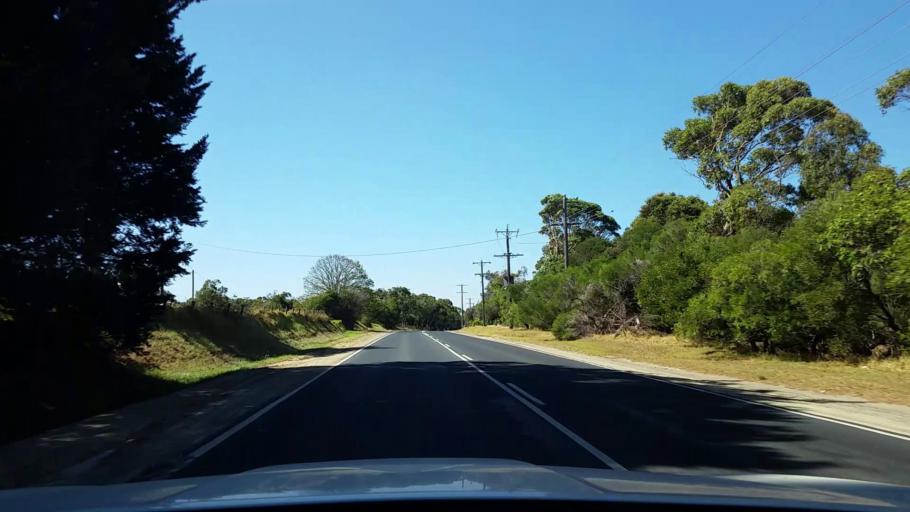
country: AU
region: Victoria
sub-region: Mornington Peninsula
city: Langwarrin South
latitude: -38.1999
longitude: 145.2080
